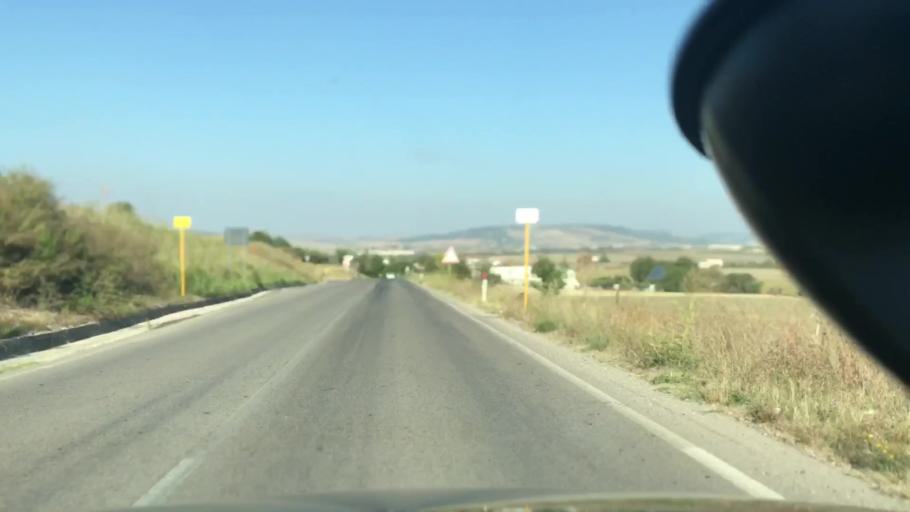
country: IT
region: Basilicate
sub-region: Provincia di Matera
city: La Martella
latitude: 40.6600
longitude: 16.5666
